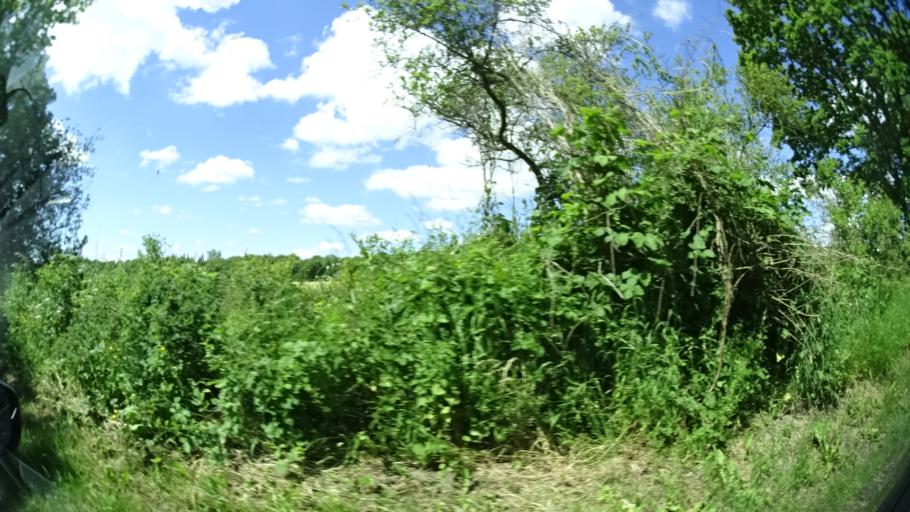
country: DK
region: Central Jutland
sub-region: Syddjurs Kommune
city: Ronde
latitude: 56.2867
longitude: 10.4802
